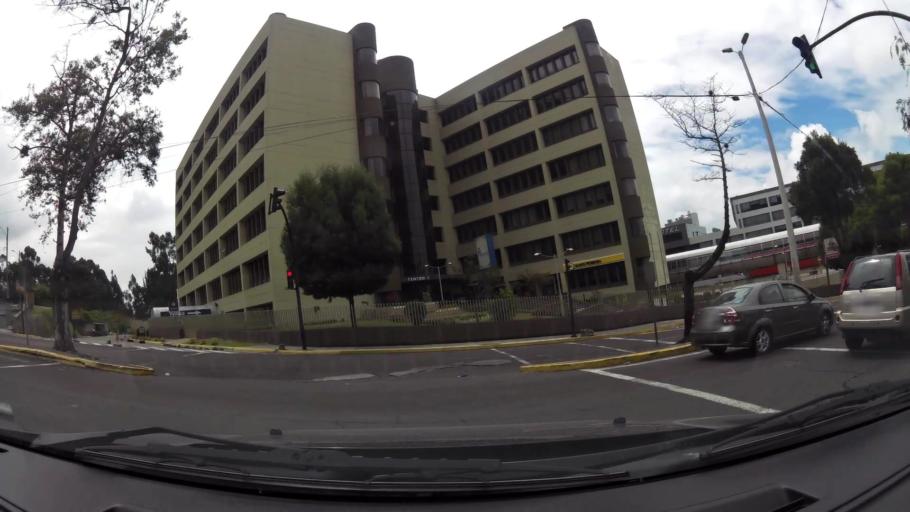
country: EC
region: Pichincha
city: Quito
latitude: -0.1830
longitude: -78.5037
